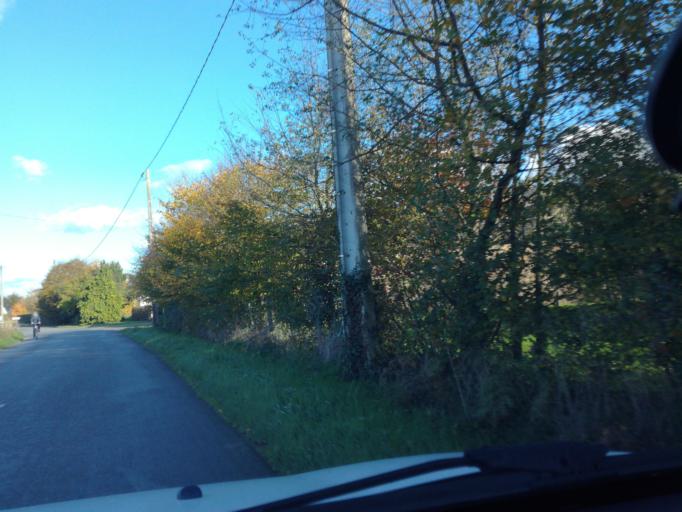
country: FR
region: Brittany
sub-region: Departement d'Ille-et-Vilaine
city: Chavagne
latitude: 48.0484
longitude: -1.8007
